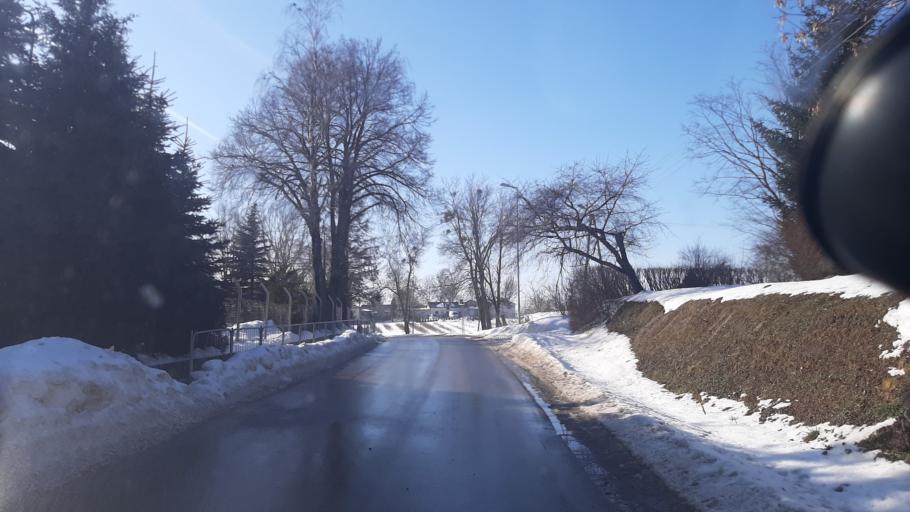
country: PL
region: Lublin Voivodeship
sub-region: Powiat lubelski
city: Garbow
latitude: 51.3128
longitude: 22.3085
